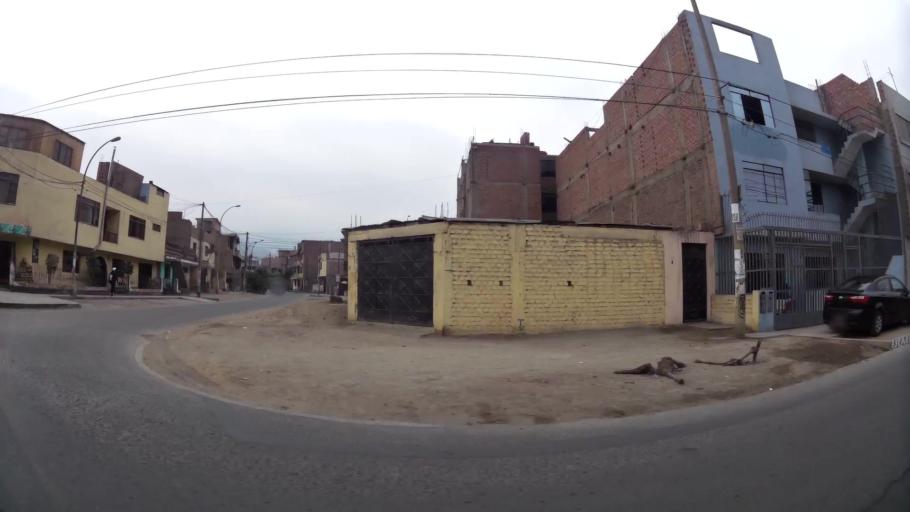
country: PE
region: Lima
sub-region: Lima
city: Independencia
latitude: -11.9897
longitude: -77.0075
